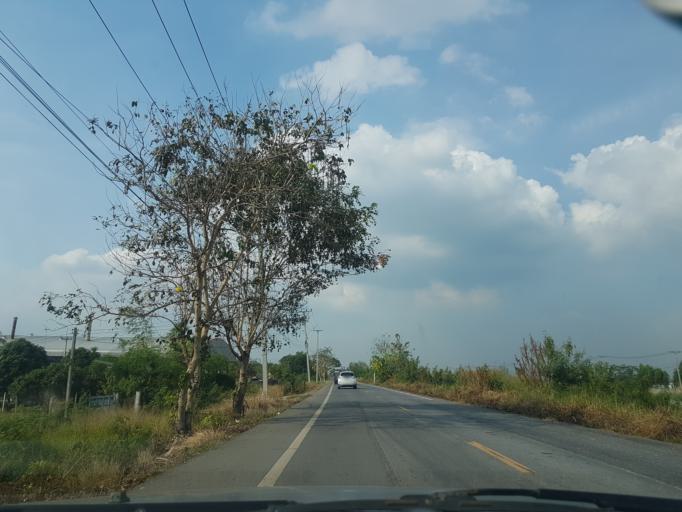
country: TH
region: Phra Nakhon Si Ayutthaya
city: Phachi
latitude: 14.4213
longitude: 100.7805
